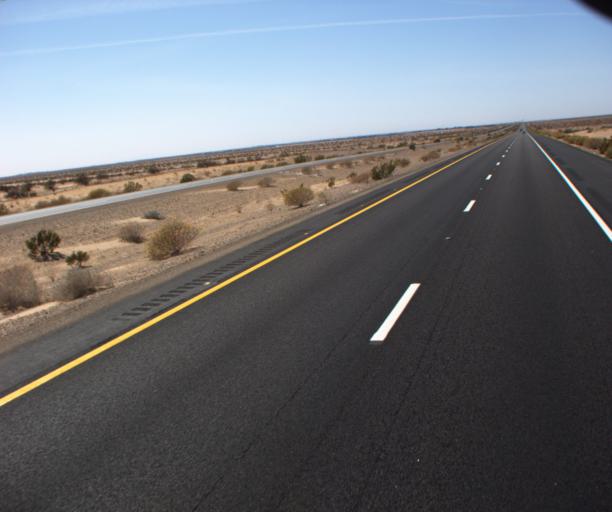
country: US
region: Arizona
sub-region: Yuma County
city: Somerton
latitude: 32.4954
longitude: -114.6101
